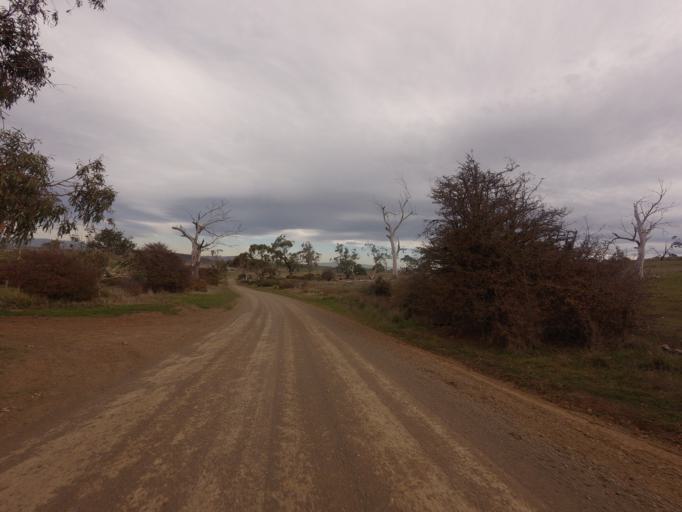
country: AU
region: Tasmania
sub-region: Derwent Valley
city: New Norfolk
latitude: -42.3888
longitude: 146.9779
